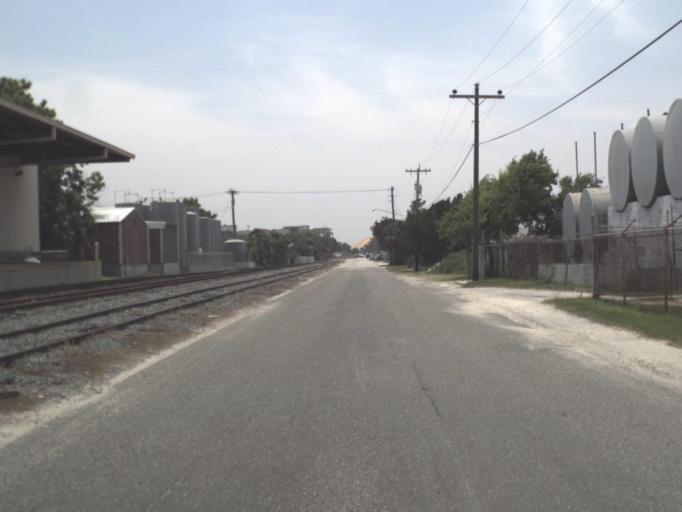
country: US
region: Florida
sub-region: Nassau County
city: Fernandina Beach
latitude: 30.6752
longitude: -81.4642
